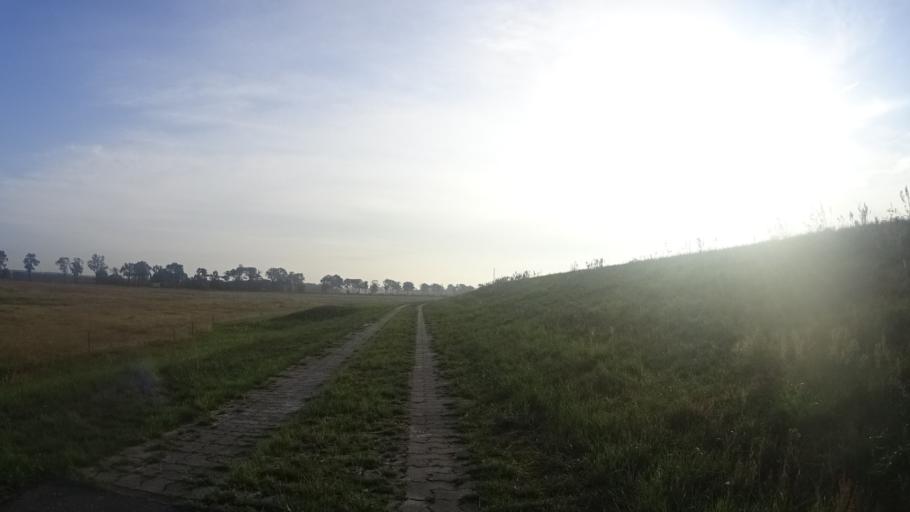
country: DE
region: Brandenburg
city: Lenzen
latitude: 53.0814
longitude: 11.4427
